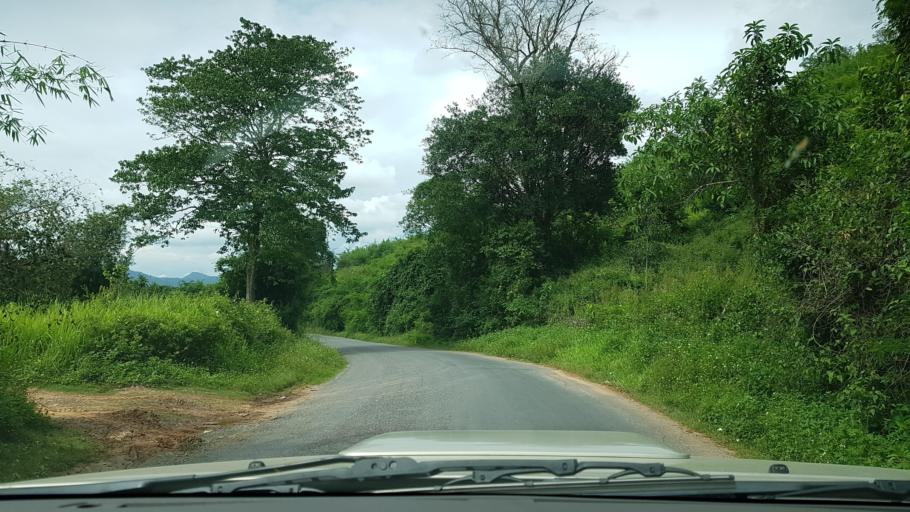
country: LA
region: Oudomxai
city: Muang Xay
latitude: 20.4121
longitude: 101.7763
